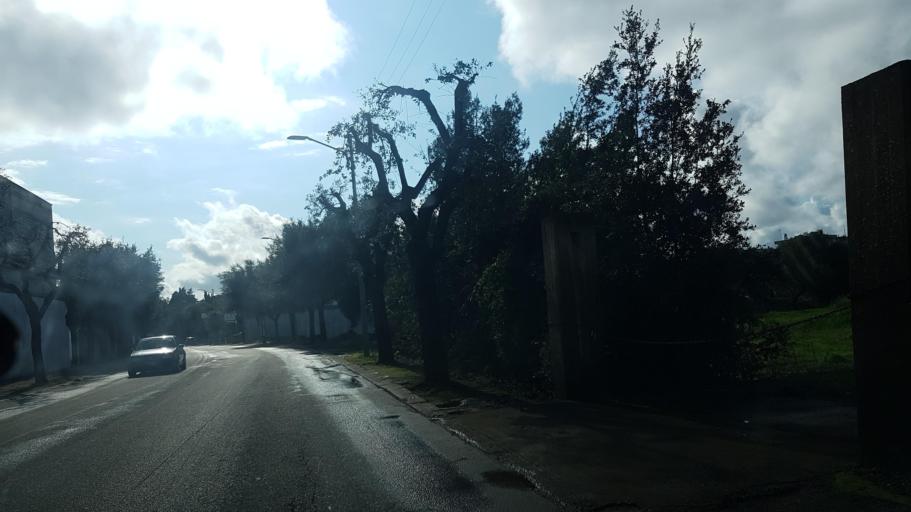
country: IT
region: Apulia
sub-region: Provincia di Brindisi
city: Carovigno
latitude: 40.7086
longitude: 17.6540
